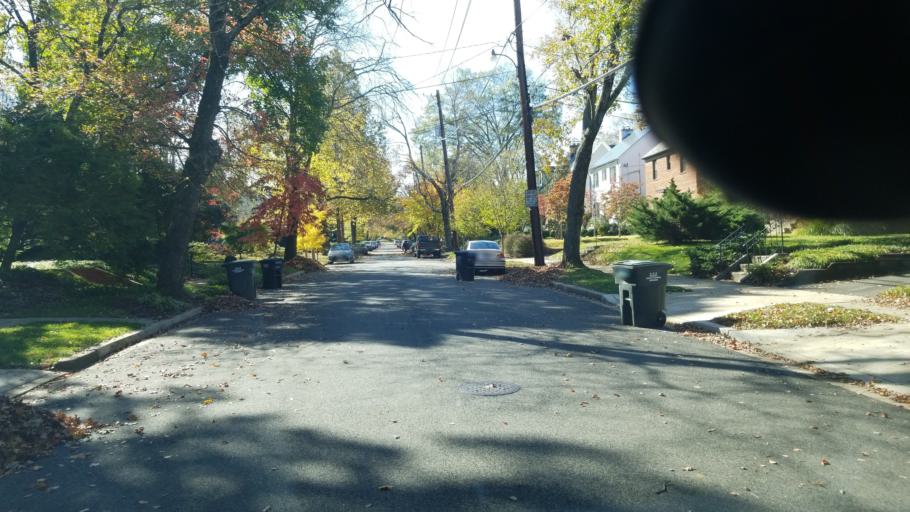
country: US
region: Maryland
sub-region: Montgomery County
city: Chevy Chase
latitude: 38.9719
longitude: -77.0572
